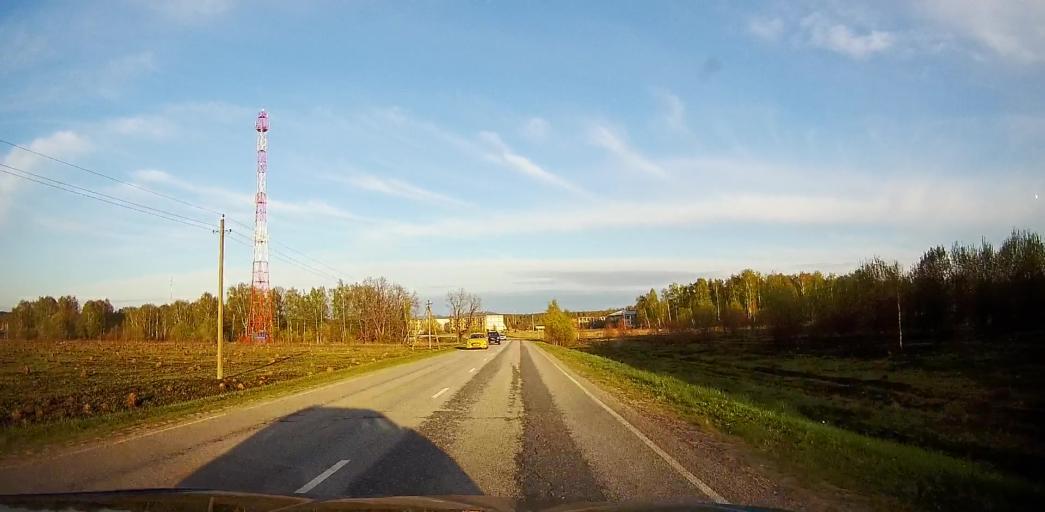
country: RU
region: Moskovskaya
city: Meshcherino
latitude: 55.2348
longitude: 38.3559
